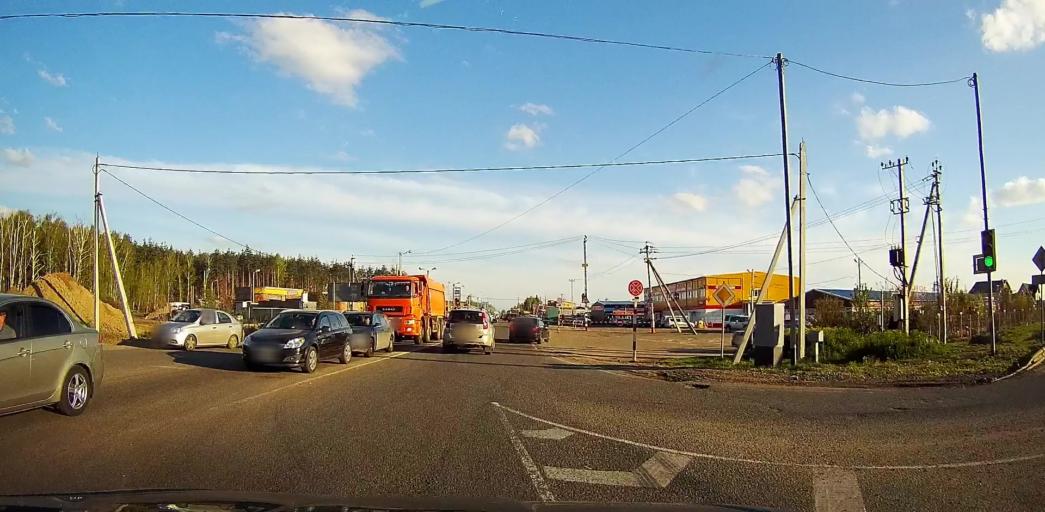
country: RU
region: Moskovskaya
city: Bronnitsy
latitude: 55.3914
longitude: 38.2044
